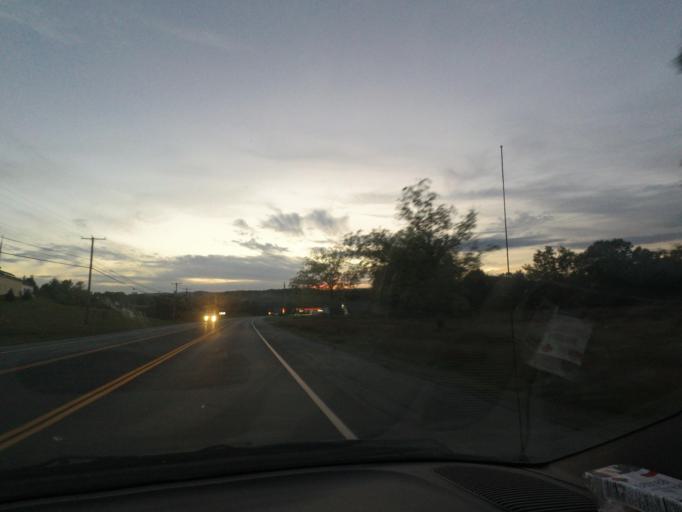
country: US
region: Vermont
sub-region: Windham County
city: Brattleboro
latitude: 42.8849
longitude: -72.5398
